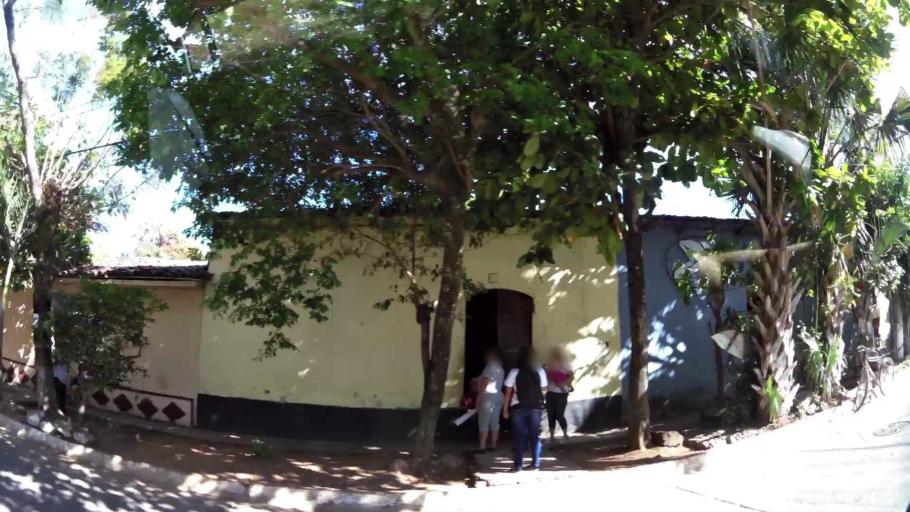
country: SV
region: Cuscatlan
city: Suchitoto
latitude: 13.9314
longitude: -89.0297
